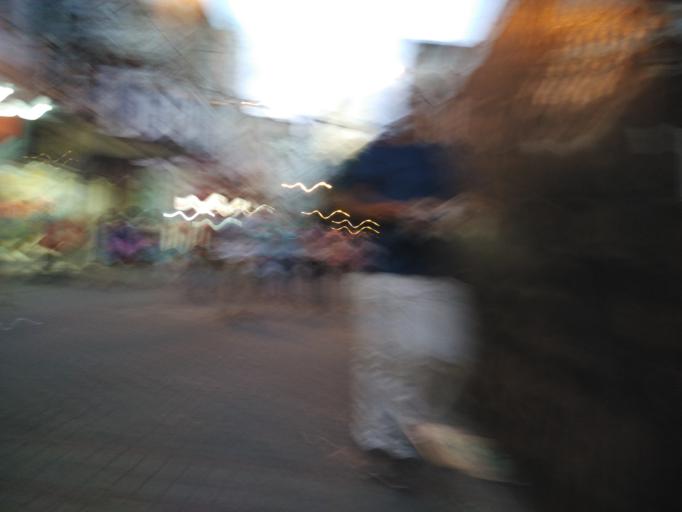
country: BR
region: Pernambuco
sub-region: Recife
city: Recife
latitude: -8.0641
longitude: -34.8803
